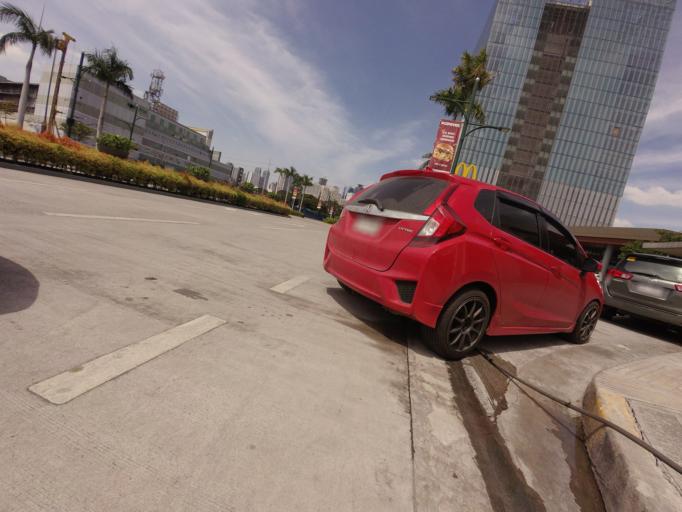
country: PH
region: Metro Manila
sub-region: Pasig
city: Pasig City
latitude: 14.5780
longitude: 121.0756
